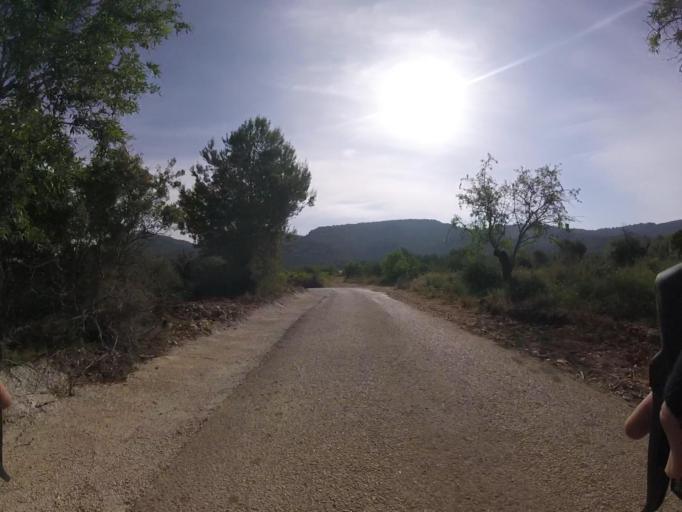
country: ES
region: Valencia
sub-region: Provincia de Castello
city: Alcala de Xivert
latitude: 40.2852
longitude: 0.2661
